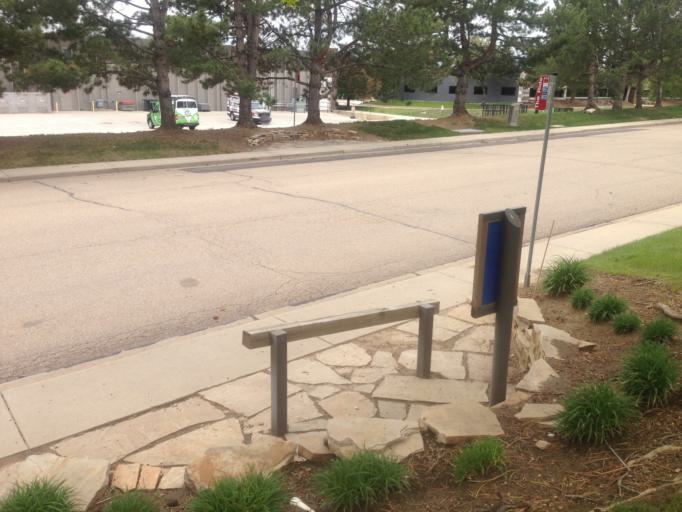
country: US
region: Colorado
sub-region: Boulder County
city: Longmont
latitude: 40.1400
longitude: -105.1229
